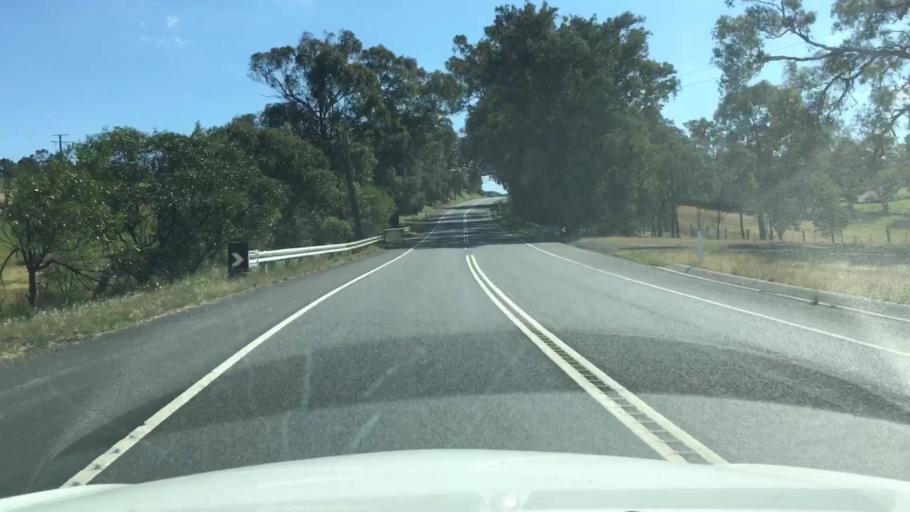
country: AU
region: Victoria
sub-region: Nillumbik
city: North Warrandyte
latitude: -37.6819
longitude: 145.2406
